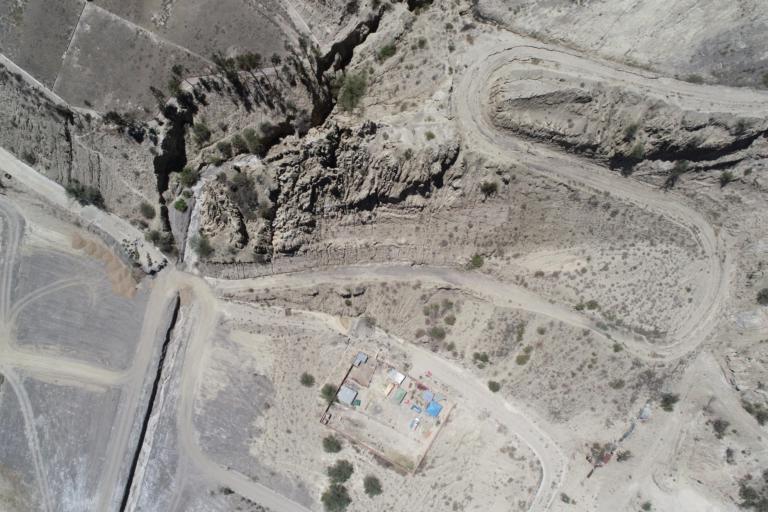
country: BO
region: La Paz
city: La Paz
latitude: -16.6196
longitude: -68.0599
